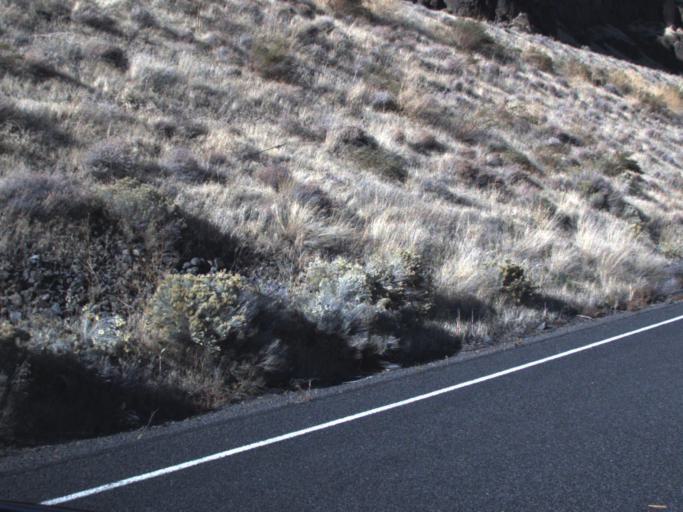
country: US
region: Washington
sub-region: Franklin County
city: Connell
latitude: 46.5494
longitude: -118.5552
